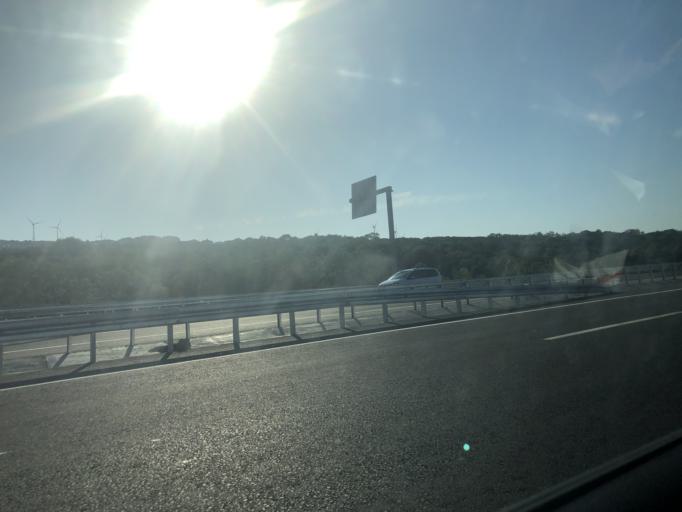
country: TR
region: Istanbul
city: Catalca
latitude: 41.1442
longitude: 28.4762
